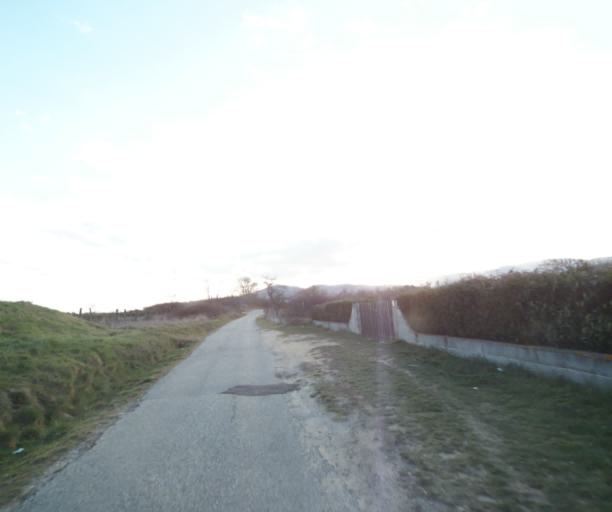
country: FR
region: Rhone-Alpes
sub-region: Departement de l'Ardeche
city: Davezieux
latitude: 45.2436
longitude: 4.7030
